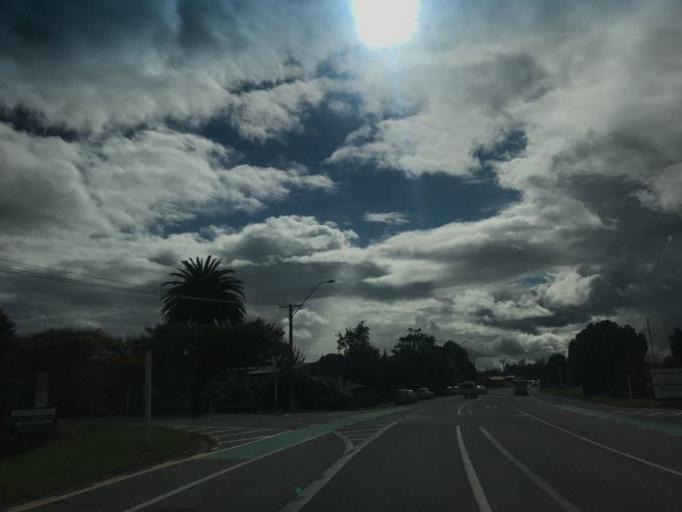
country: NZ
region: Wellington
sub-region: Kapiti Coast District
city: Otaki
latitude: -40.7695
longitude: 175.1455
